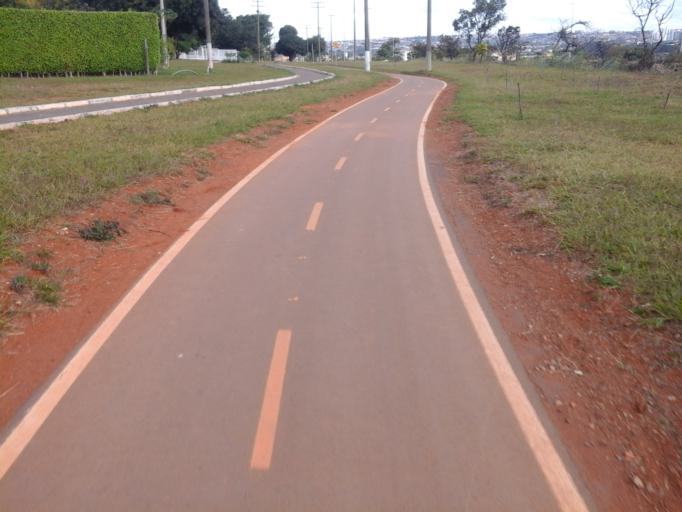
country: BR
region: Federal District
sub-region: Brasilia
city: Brasilia
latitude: -15.8138
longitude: -47.9922
